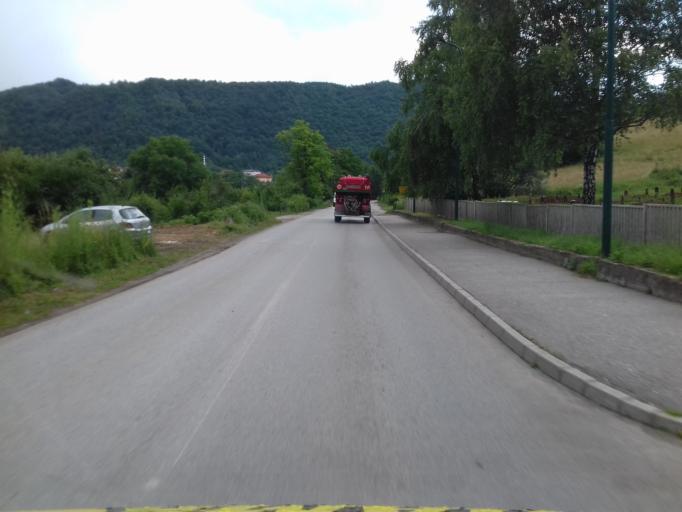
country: BA
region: Federation of Bosnia and Herzegovina
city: Visoko
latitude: 43.9755
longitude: 18.1875
